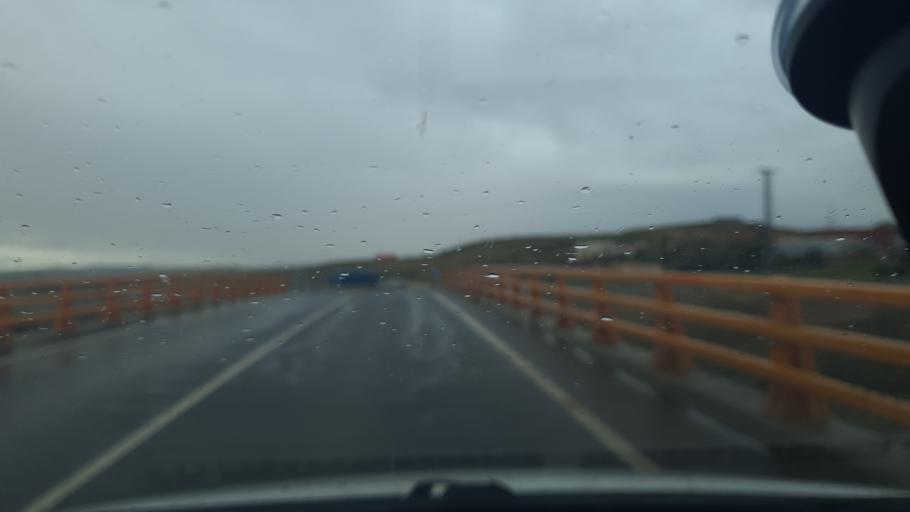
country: ES
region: Castille and Leon
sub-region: Provincia de Segovia
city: Carbonero el Mayor
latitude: 41.1118
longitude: -4.2544
